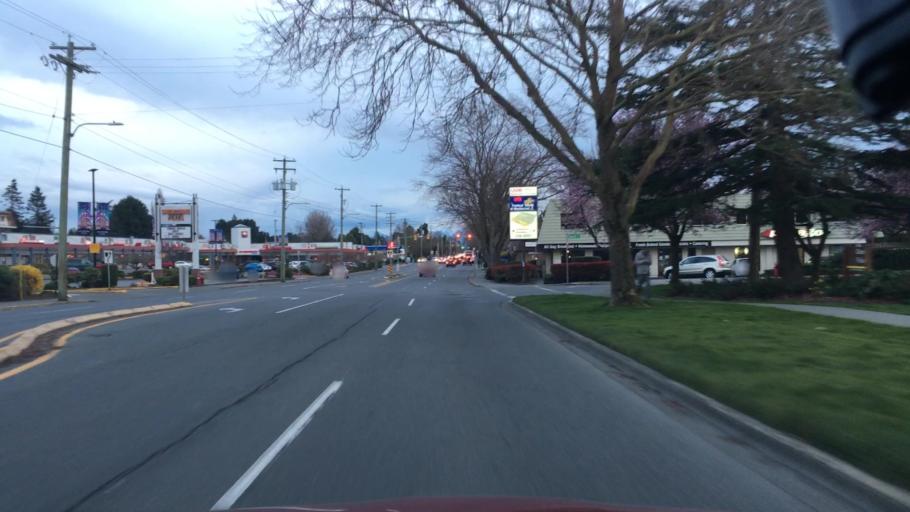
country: CA
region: British Columbia
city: Oak Bay
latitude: 48.4607
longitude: -123.3330
